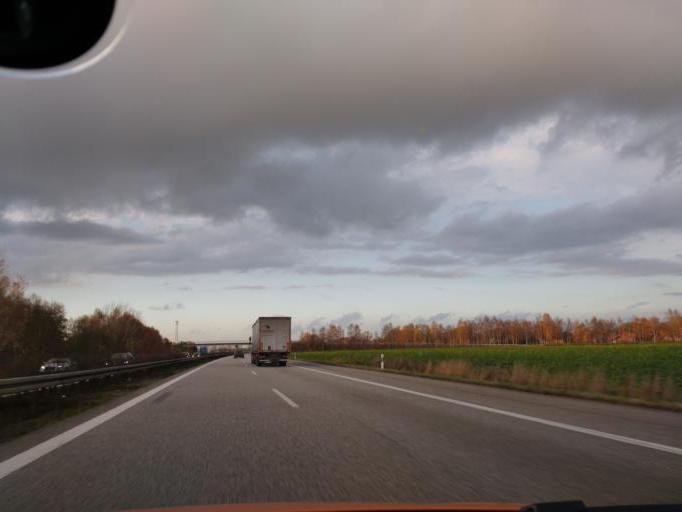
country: DE
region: Mecklenburg-Vorpommern
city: Neustadt-Glewe
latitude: 53.4008
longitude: 11.5784
